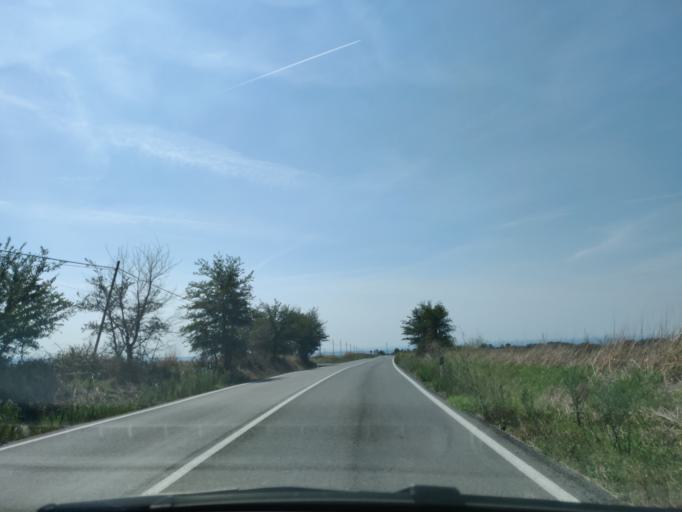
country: IT
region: Latium
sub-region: Provincia di Viterbo
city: Tarquinia
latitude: 42.2449
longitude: 11.8086
